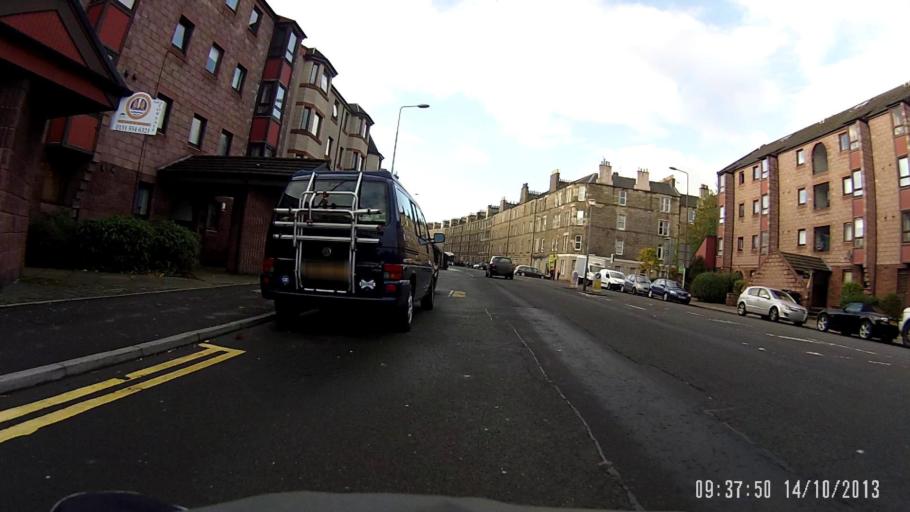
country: GB
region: Scotland
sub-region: West Lothian
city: Seafield
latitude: 55.9676
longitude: -3.1688
